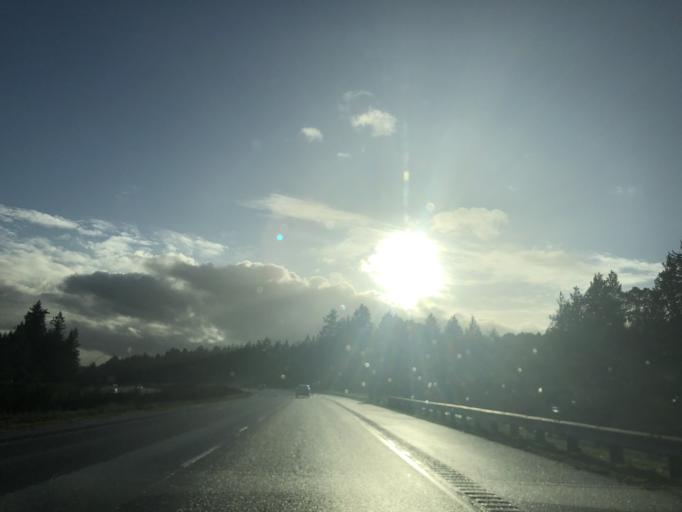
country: US
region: Washington
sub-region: Kitsap County
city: Silverdale
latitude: 47.6359
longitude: -122.7087
